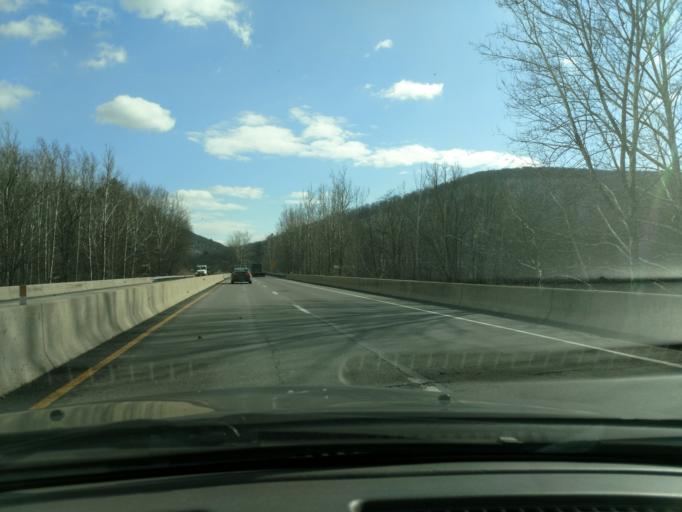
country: US
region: Pennsylvania
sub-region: Berks County
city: West Hamburg
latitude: 40.6064
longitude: -76.0299
